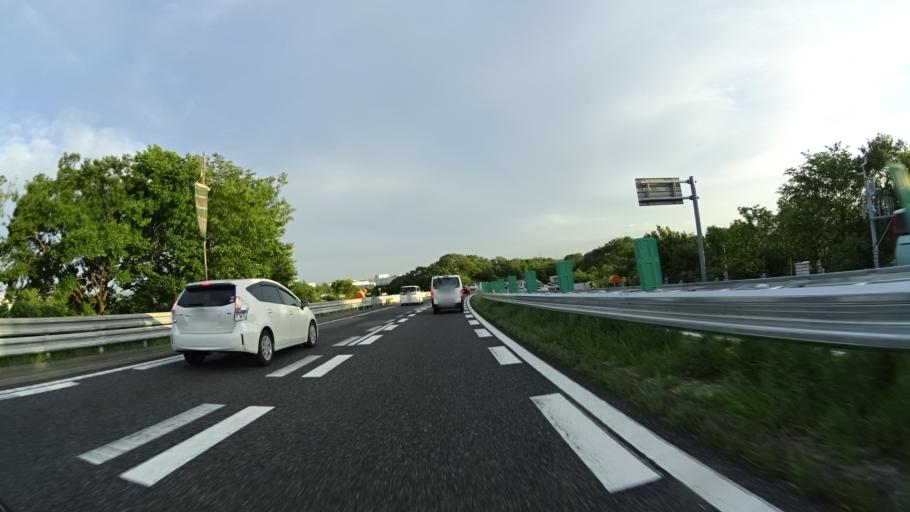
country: JP
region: Aichi
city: Kasugai
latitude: 35.3168
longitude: 137.0197
